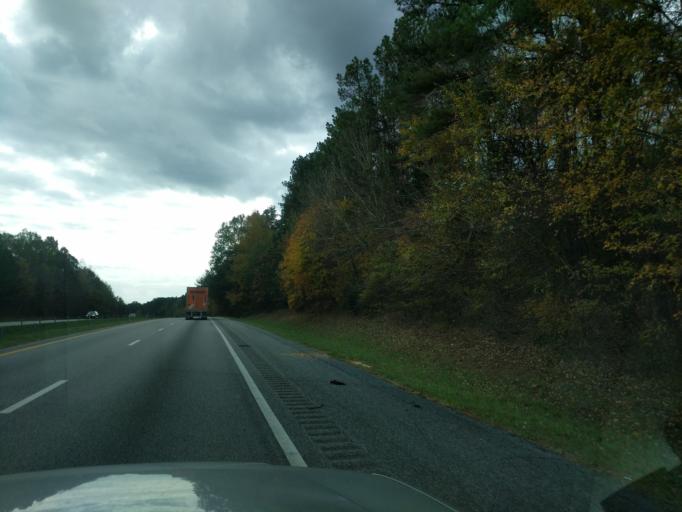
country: US
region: South Carolina
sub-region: Laurens County
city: Clinton
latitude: 34.5342
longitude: -81.8834
